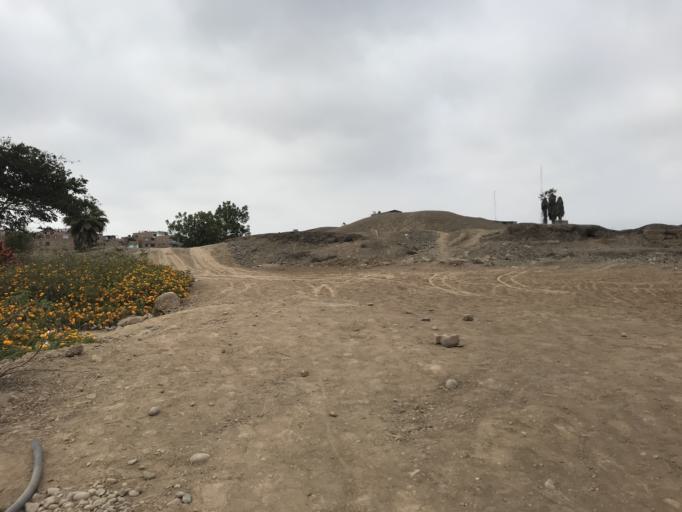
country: PE
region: Callao
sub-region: Callao
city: Callao
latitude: -12.0668
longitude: -77.0839
